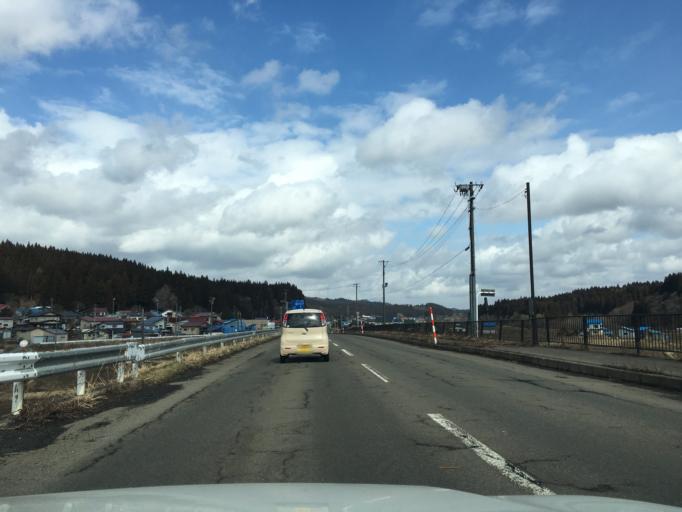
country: JP
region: Akita
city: Takanosu
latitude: 40.0302
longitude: 140.2743
